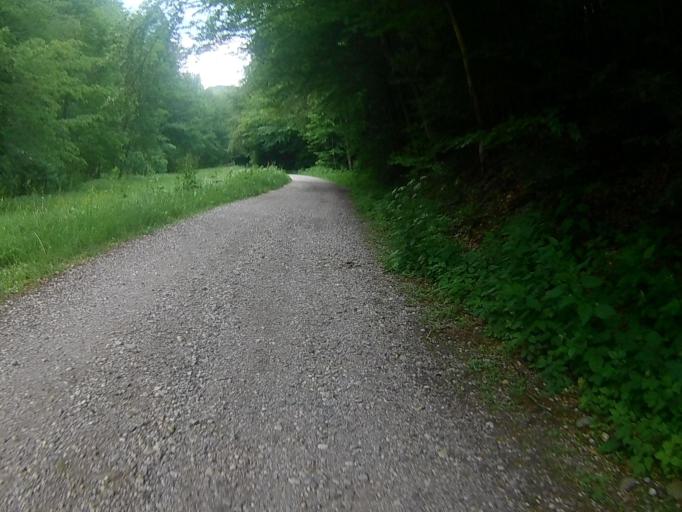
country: SI
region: Maribor
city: Bresternica
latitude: 46.6010
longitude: 15.5897
